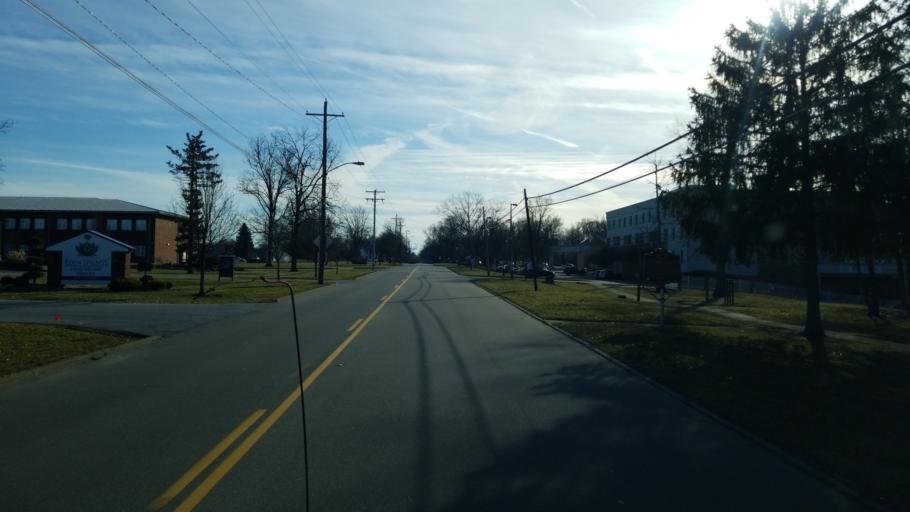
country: US
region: Ohio
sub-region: Sandusky County
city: Green Springs
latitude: 41.2639
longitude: -83.0519
